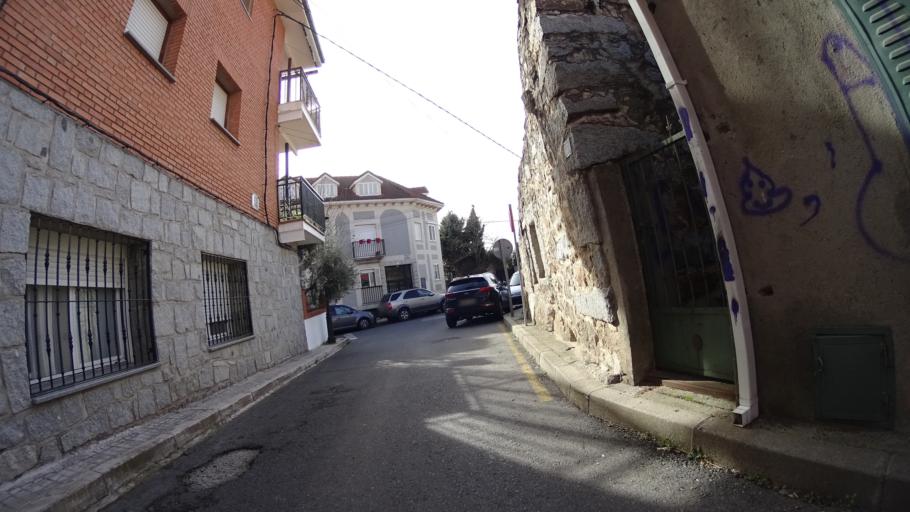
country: ES
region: Madrid
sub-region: Provincia de Madrid
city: Moralzarzal
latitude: 40.6795
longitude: -3.9738
